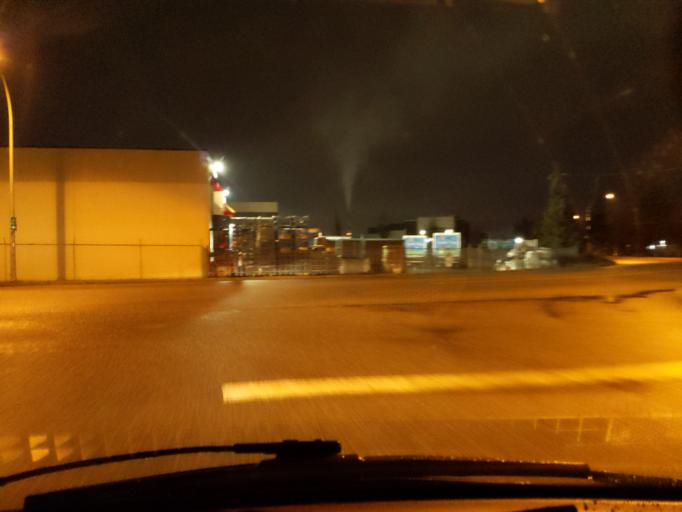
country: CA
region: British Columbia
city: Walnut Grove
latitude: 49.1778
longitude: -122.6735
